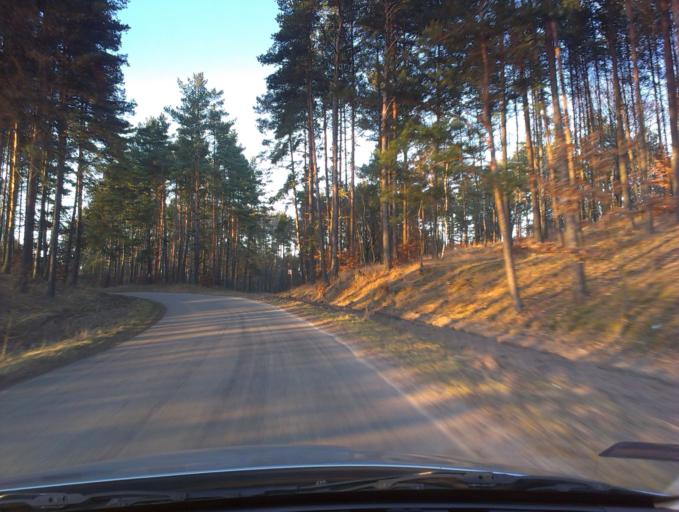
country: PL
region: West Pomeranian Voivodeship
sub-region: Powiat szczecinecki
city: Lubowo
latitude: 53.6191
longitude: 16.3744
